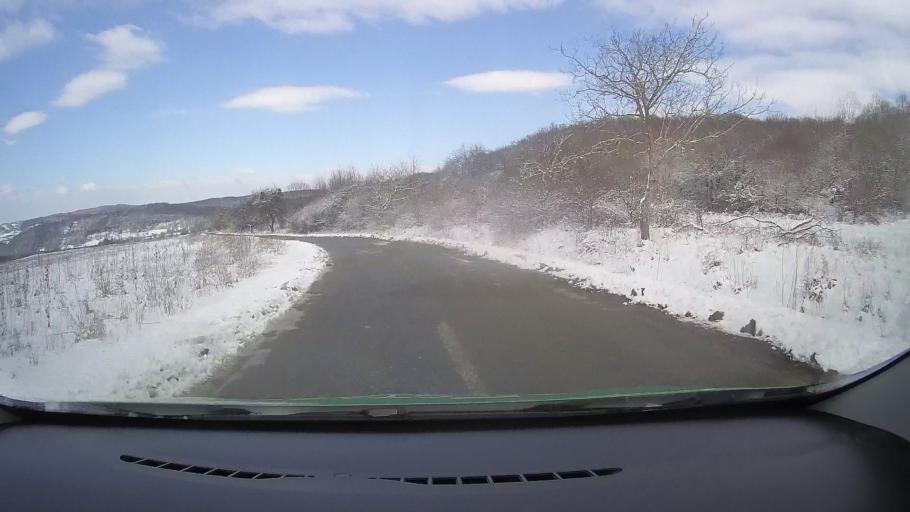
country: RO
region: Sibiu
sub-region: Comuna Mihaileni
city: Mihaileni
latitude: 46.0036
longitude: 24.4261
